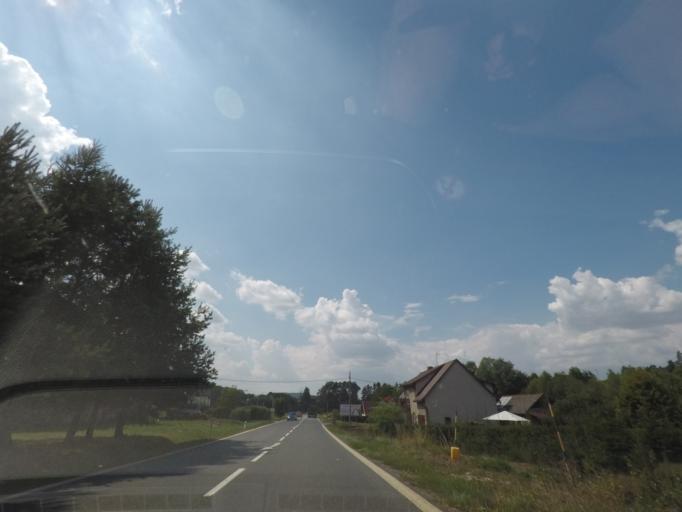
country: CZ
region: Kralovehradecky
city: Pilnikov
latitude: 50.5246
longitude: 15.7869
